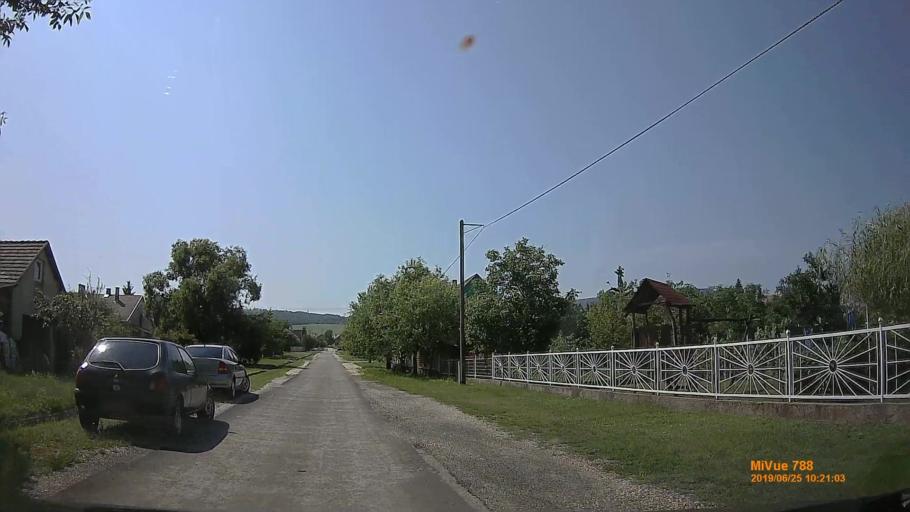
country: HU
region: Komarom-Esztergom
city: Dorog
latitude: 47.7364
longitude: 18.6994
